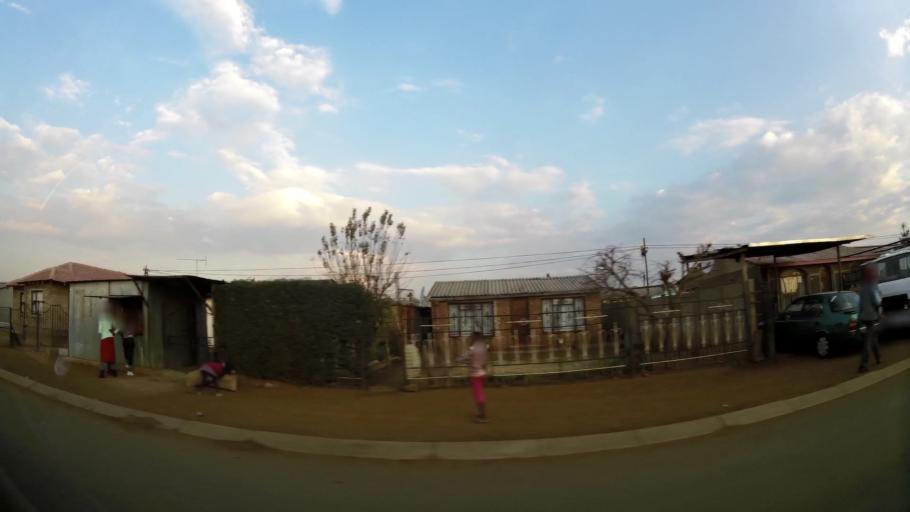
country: ZA
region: Gauteng
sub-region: City of Johannesburg Metropolitan Municipality
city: Orange Farm
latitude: -26.5477
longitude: 27.8686
